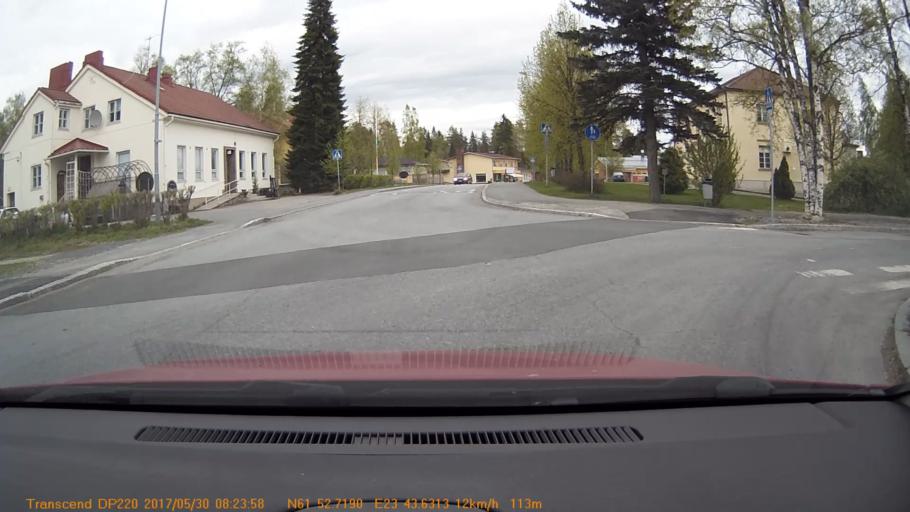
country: FI
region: Pirkanmaa
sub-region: Tampere
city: Kuru
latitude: 61.8786
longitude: 23.7272
